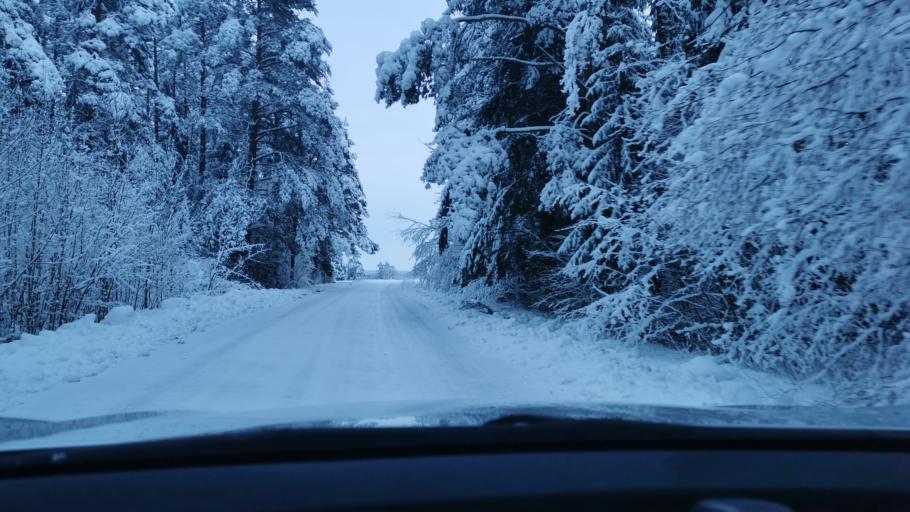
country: EE
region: Laeaene-Virumaa
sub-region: Haljala vald
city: Haljala
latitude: 59.4957
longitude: 26.3109
